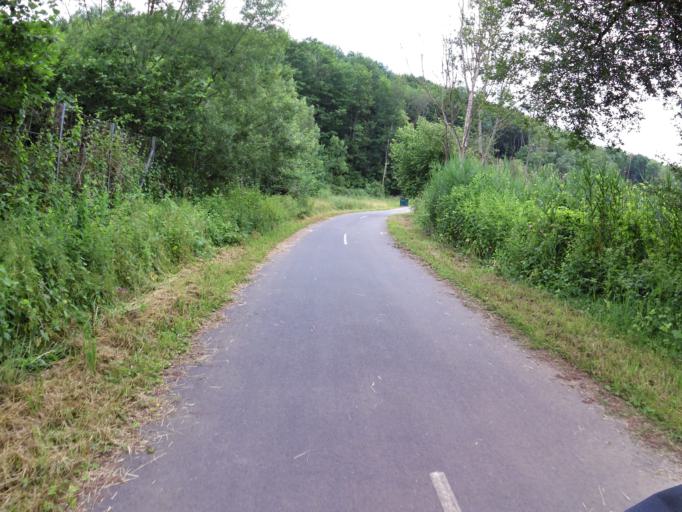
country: FR
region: Champagne-Ardenne
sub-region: Departement des Ardennes
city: Donchery
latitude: 49.7013
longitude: 4.8993
